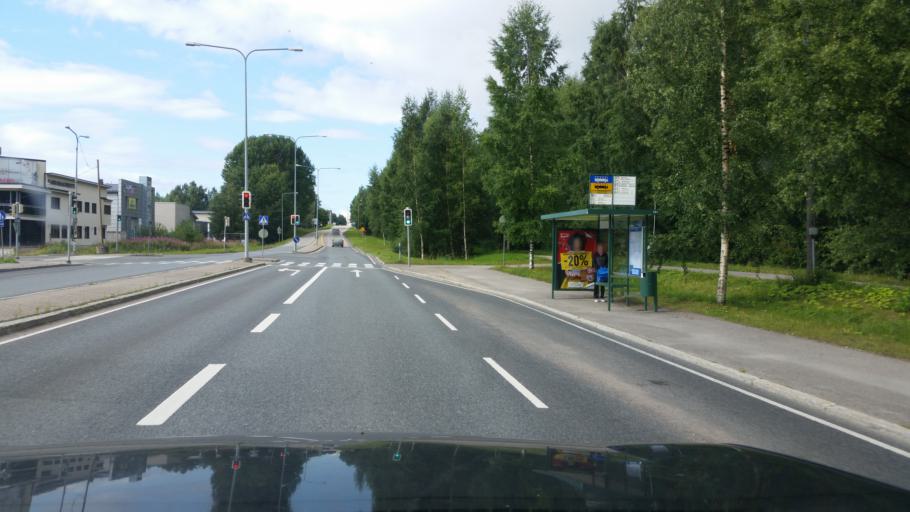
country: FI
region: Uusimaa
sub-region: Helsinki
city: Vantaa
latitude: 60.2278
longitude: 25.1220
